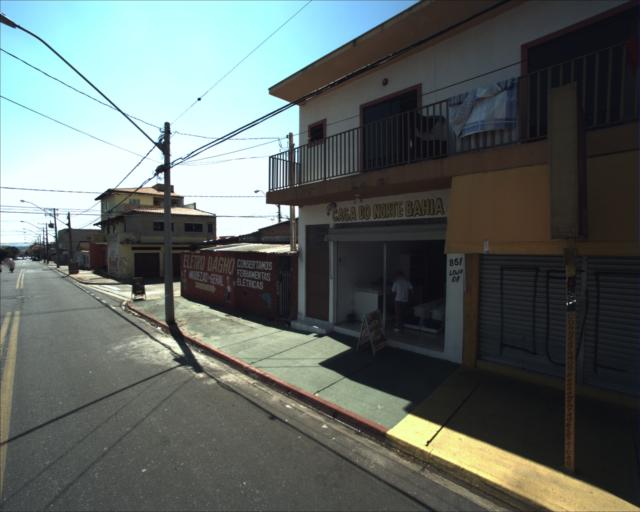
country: BR
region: Sao Paulo
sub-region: Sorocaba
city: Sorocaba
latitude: -23.5062
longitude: -47.5188
